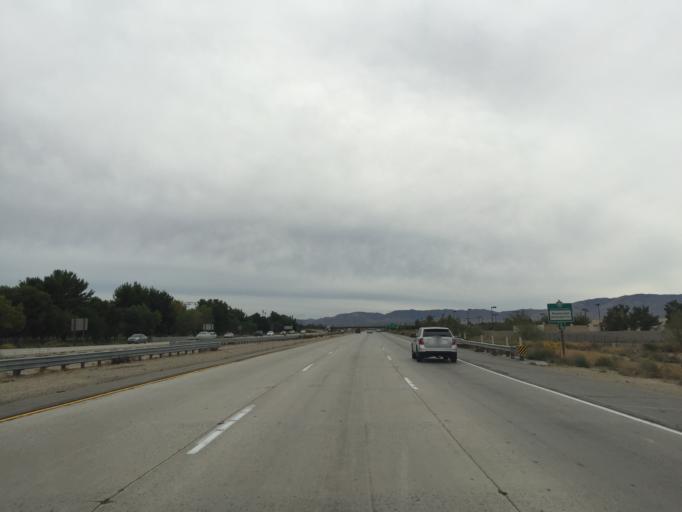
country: US
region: California
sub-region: Los Angeles County
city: Lancaster
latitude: 34.6672
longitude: -118.1537
